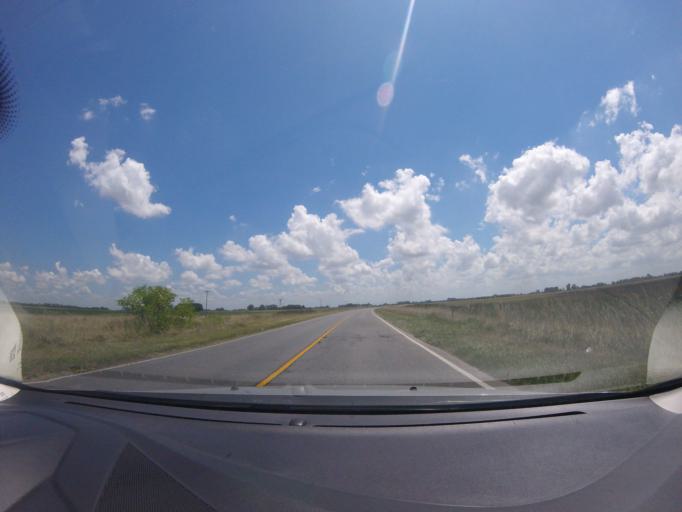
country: AR
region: Buenos Aires
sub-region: Partido de Las Flores
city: Las Flores
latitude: -36.0811
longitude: -59.0909
